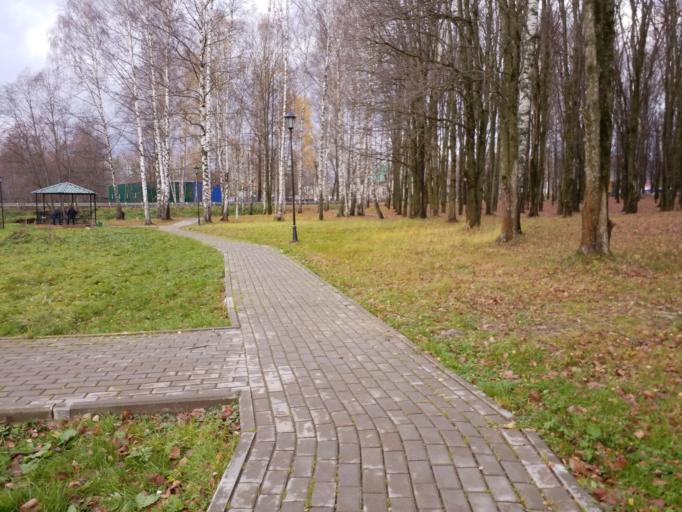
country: RU
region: Moskovskaya
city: Ashukino
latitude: 56.1608
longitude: 37.9432
